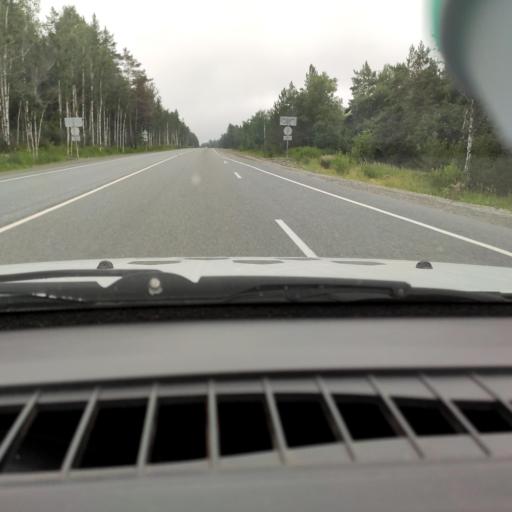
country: RU
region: Chelyabinsk
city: Zlatoust
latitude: 55.0380
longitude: 59.7241
